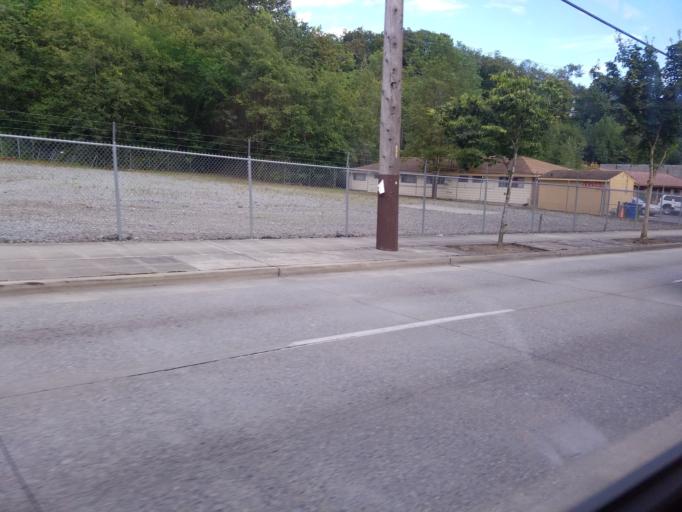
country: US
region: Washington
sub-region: King County
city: Riverton
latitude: 47.5198
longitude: -122.2798
